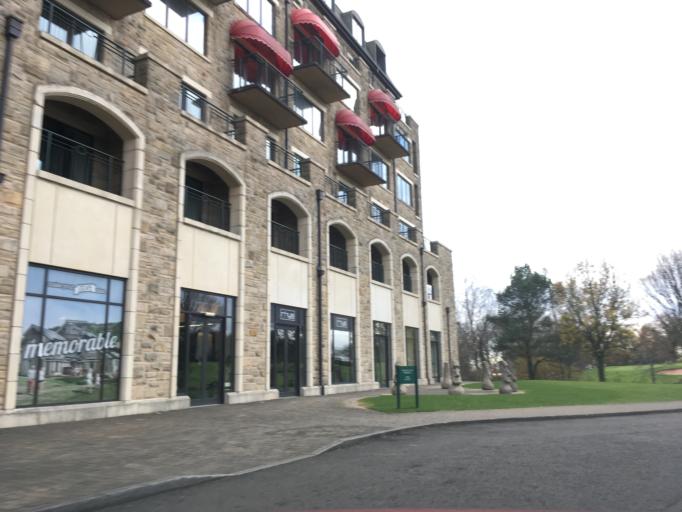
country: GB
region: Wales
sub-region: Newport
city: Langstone
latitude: 51.6028
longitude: -2.9328
